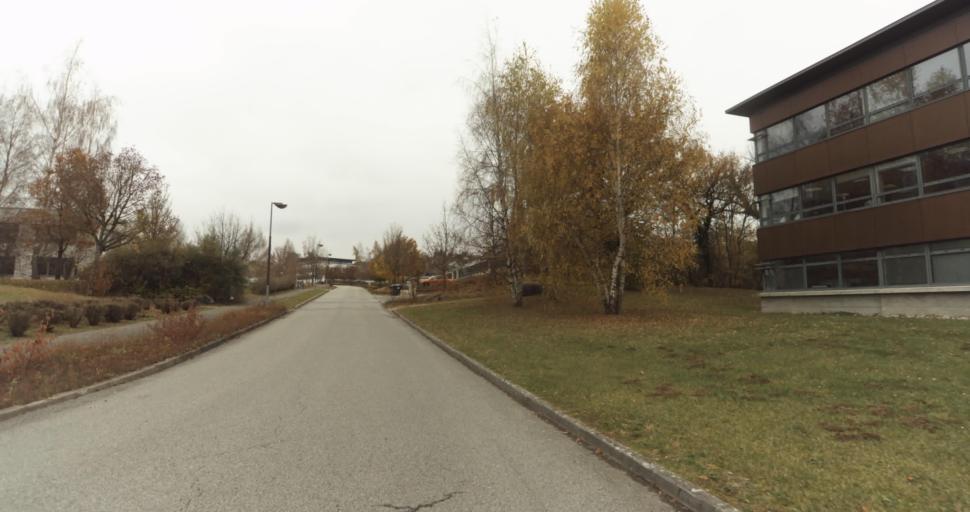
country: FR
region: Rhone-Alpes
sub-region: Departement de la Haute-Savoie
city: Seynod
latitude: 45.8989
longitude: 6.0807
